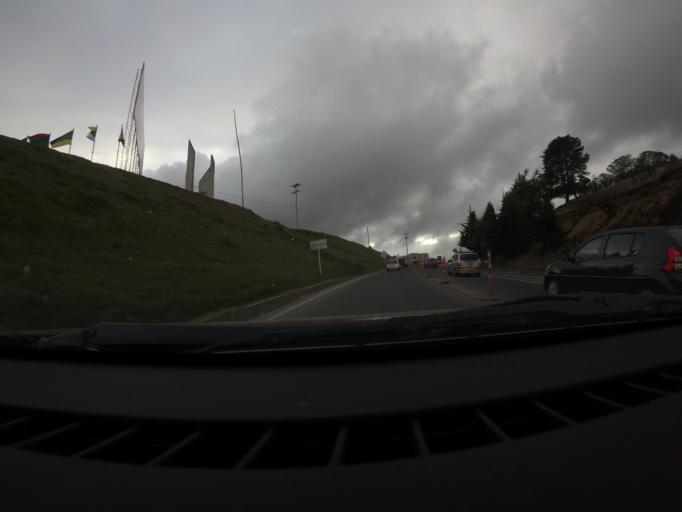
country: CO
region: Boyaca
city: Samaca
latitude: 5.4476
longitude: -73.4329
